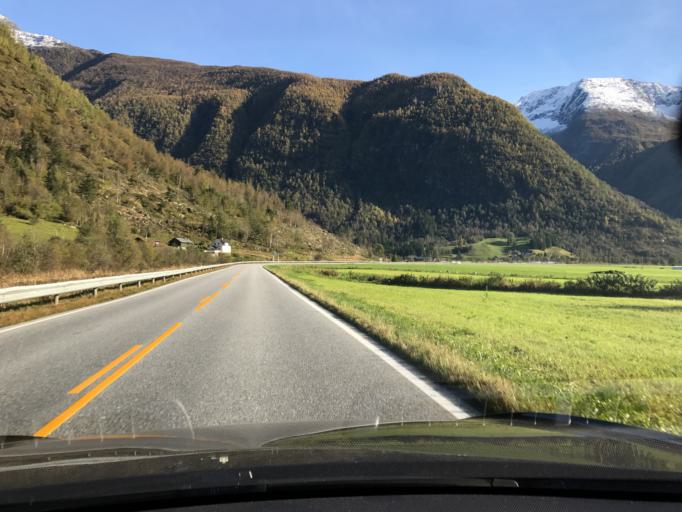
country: NO
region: Sogn og Fjordane
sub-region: Leikanger
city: Hermansverk
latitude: 61.4386
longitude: 6.7579
